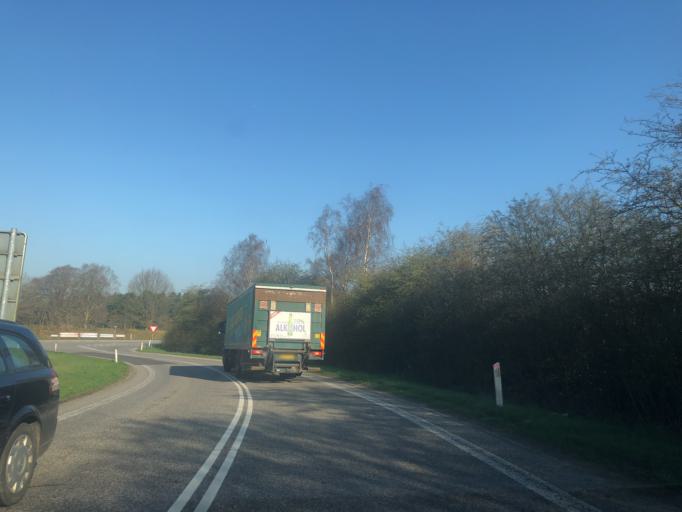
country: DK
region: Zealand
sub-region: Faxe Kommune
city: Fakse
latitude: 55.2572
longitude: 12.0981
